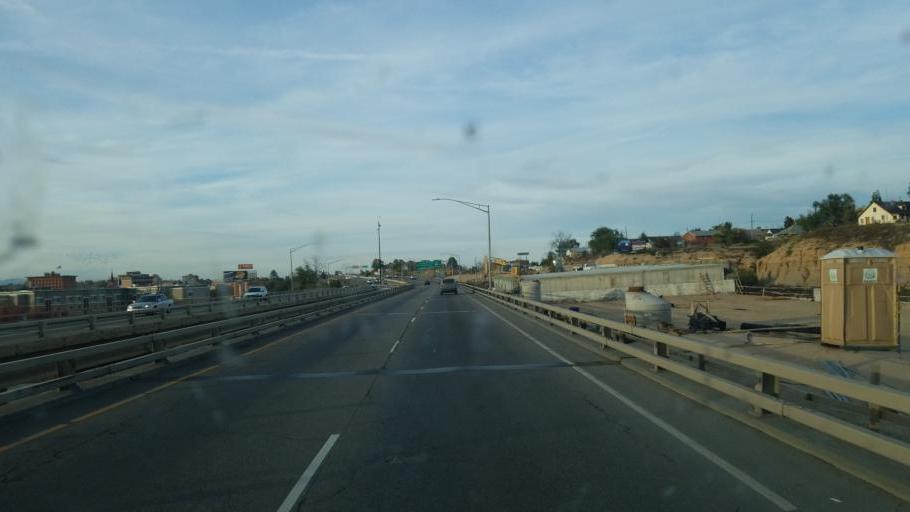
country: US
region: Colorado
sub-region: Pueblo County
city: Pueblo
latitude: 38.2641
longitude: -104.6050
